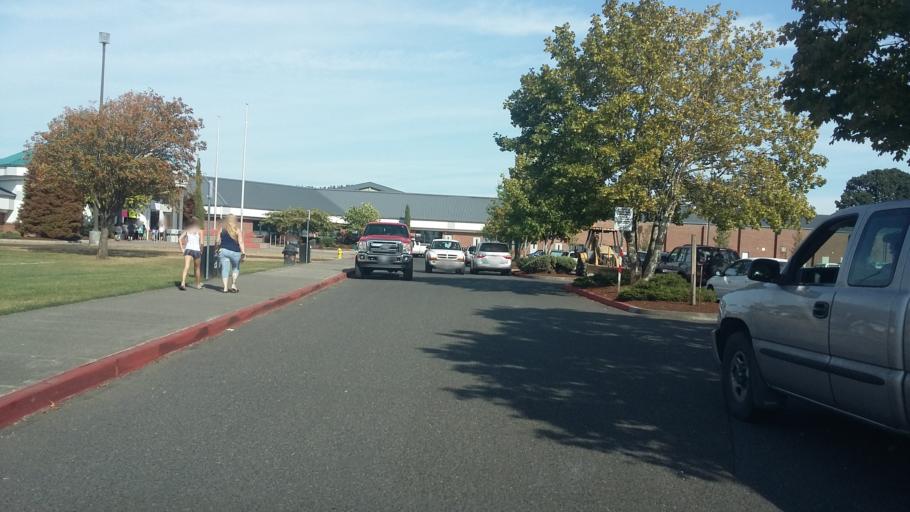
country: US
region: Washington
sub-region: Clark County
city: Battle Ground
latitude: 45.7822
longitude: -122.5421
